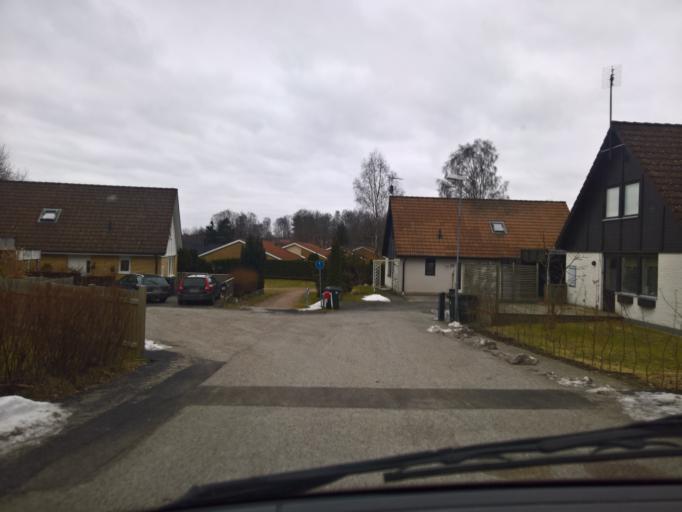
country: SE
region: Skane
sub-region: Hoors Kommun
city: Hoeoer
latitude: 55.9240
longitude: 13.5319
